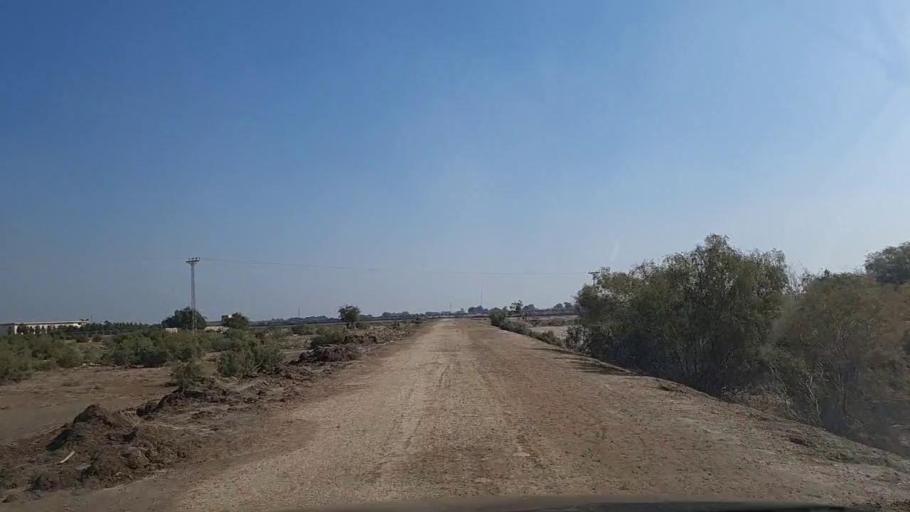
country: PK
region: Sindh
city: Nawabshah
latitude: 26.3187
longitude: 68.3477
